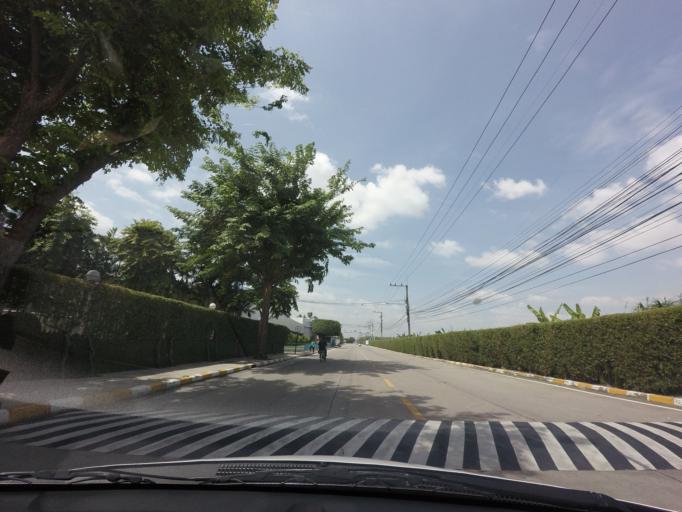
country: TH
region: Pathum Thani
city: Thanyaburi
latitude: 13.9885
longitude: 100.6745
